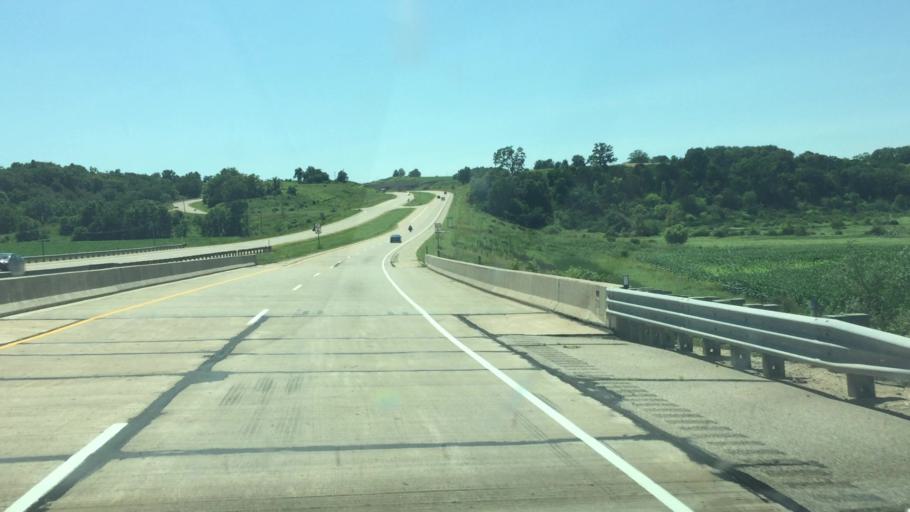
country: US
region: Wisconsin
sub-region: Iowa County
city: Mineral Point
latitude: 42.8251
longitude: -90.2408
